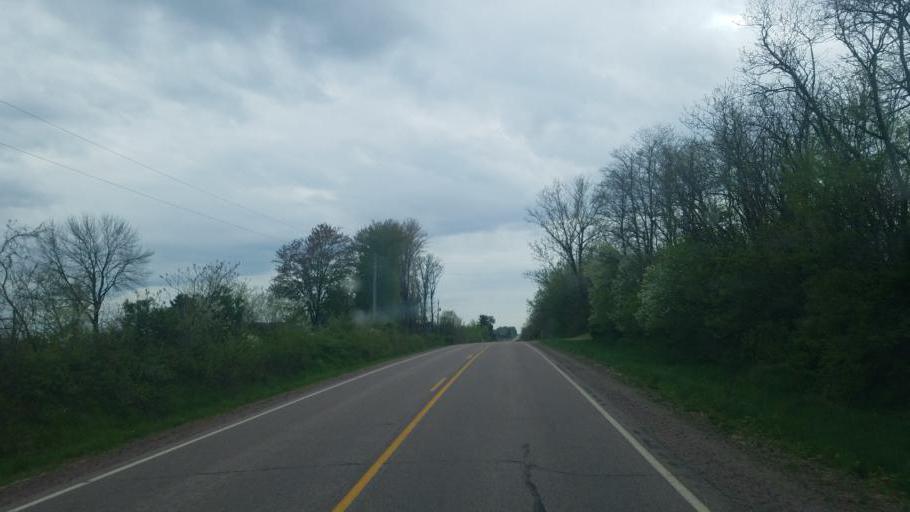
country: US
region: Wisconsin
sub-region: Wood County
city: Marshfield
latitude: 44.5737
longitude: -90.2996
